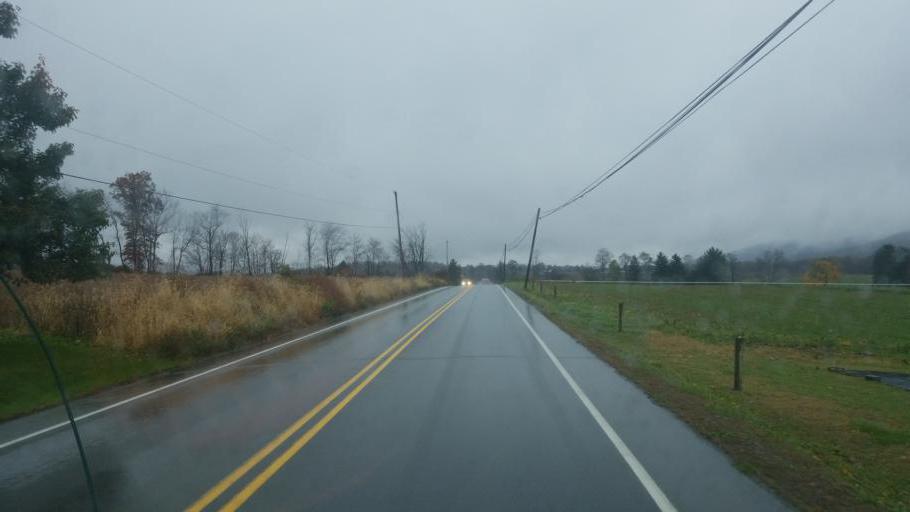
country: US
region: Pennsylvania
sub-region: Clinton County
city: Mill Hall
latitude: 41.0955
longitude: -77.5255
